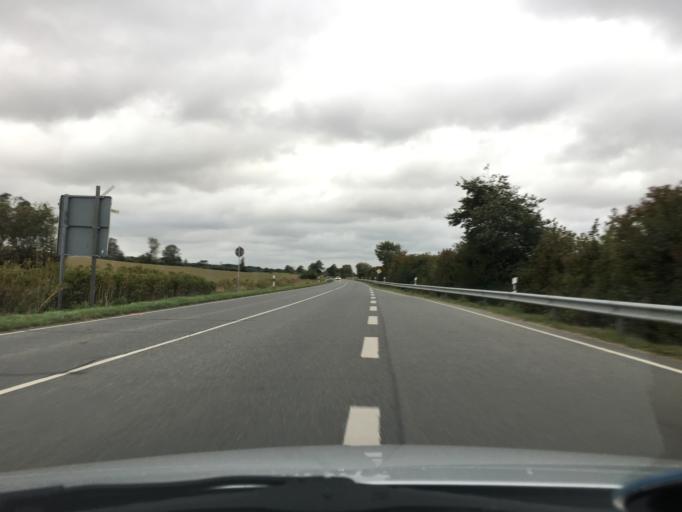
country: DE
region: Schleswig-Holstein
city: Felm
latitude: 54.4676
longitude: 10.0675
